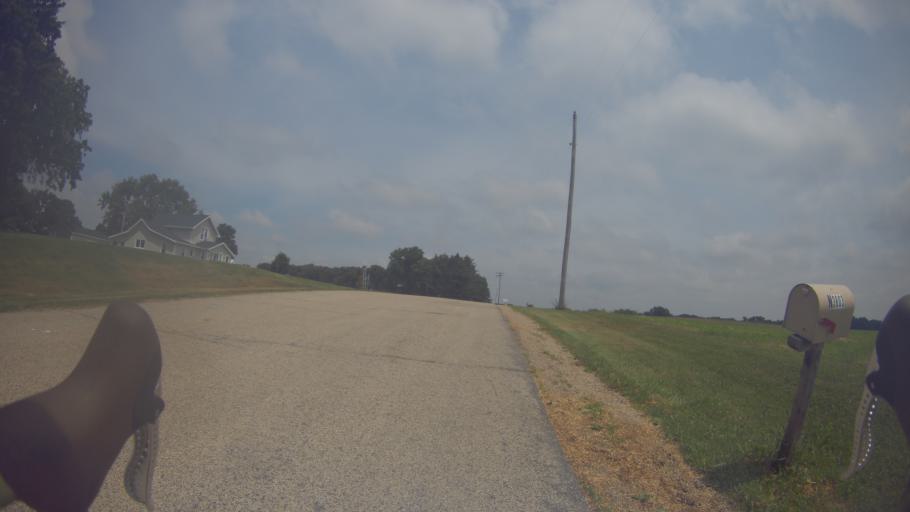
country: US
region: Wisconsin
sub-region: Jefferson County
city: Lake Ripley
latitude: 42.9830
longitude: -88.9986
